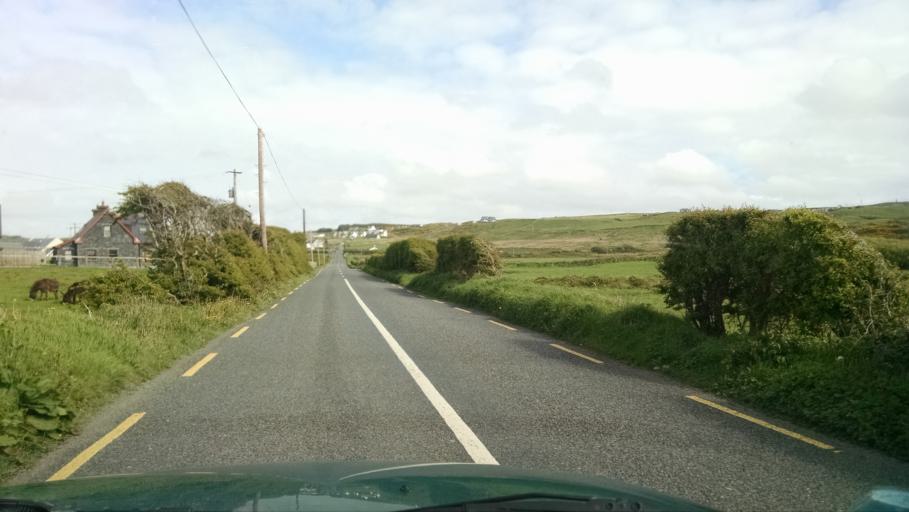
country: IE
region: Connaught
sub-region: County Galway
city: Bearna
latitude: 53.0126
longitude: -9.3698
